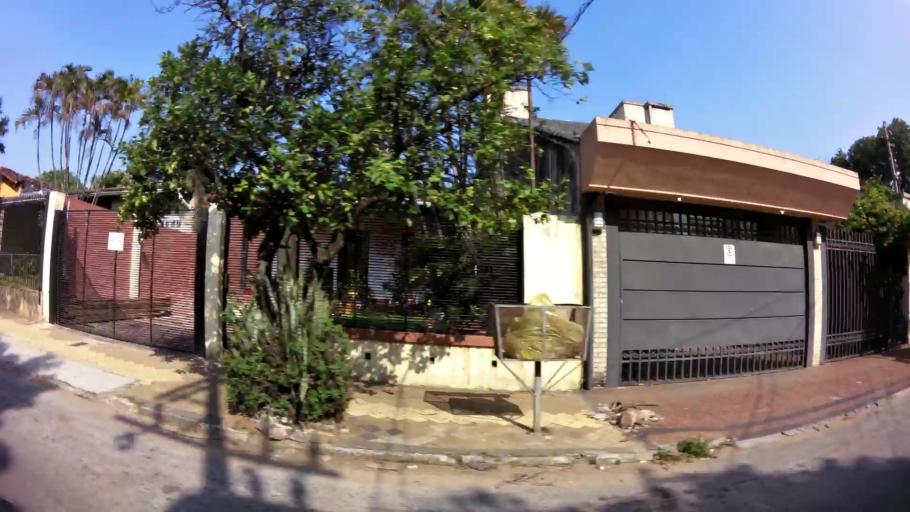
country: PY
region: Asuncion
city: Asuncion
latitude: -25.3124
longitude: -57.6267
